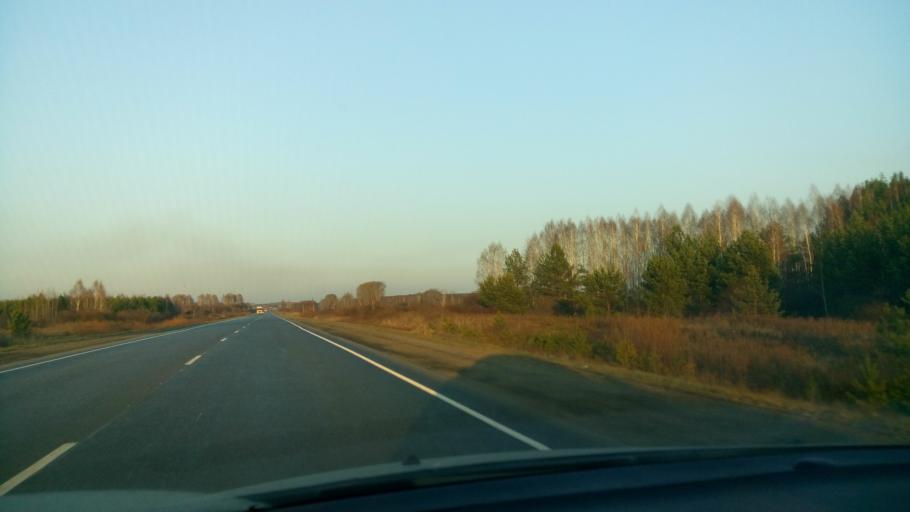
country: RU
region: Sverdlovsk
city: Obukhovskoye
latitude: 56.8286
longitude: 62.5617
